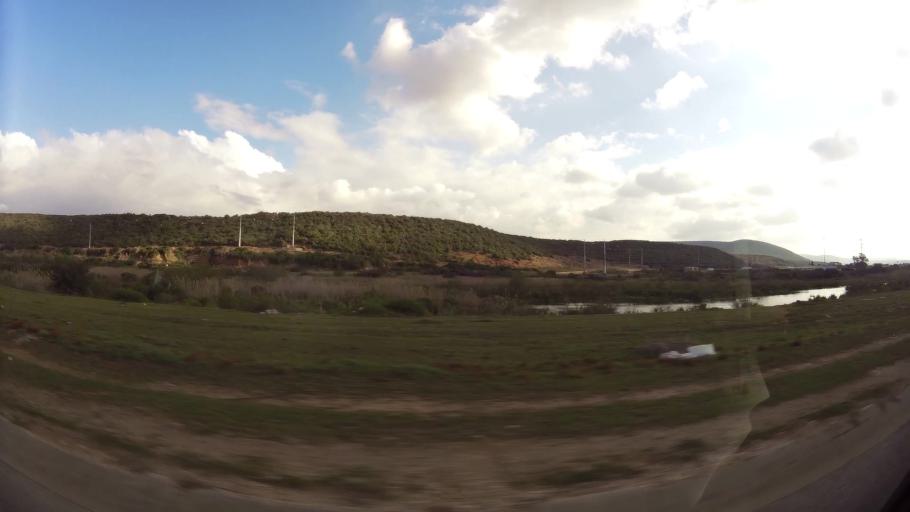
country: ZA
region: Eastern Cape
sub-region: Nelson Mandela Bay Metropolitan Municipality
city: Uitenhage
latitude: -33.7798
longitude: 25.3934
